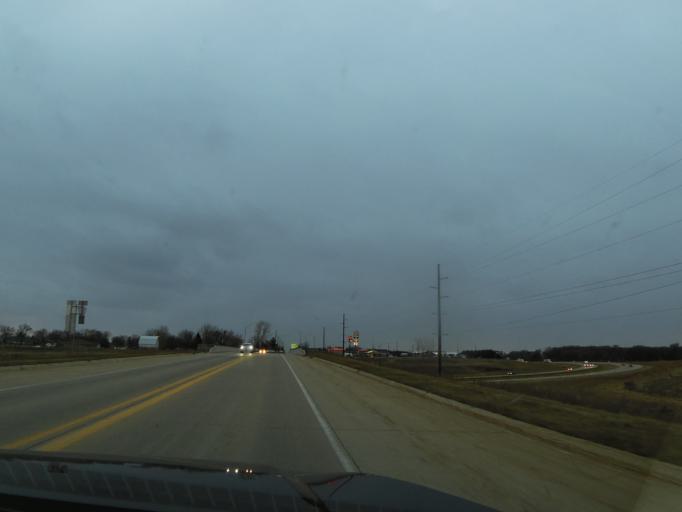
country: US
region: Iowa
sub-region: Bremer County
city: Waverly
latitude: 42.6495
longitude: -92.4502
